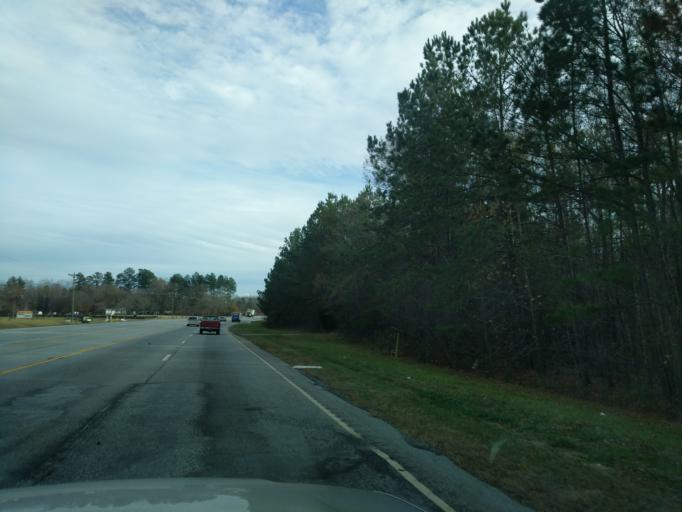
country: US
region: South Carolina
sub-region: Anderson County
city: Williamston
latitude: 34.6062
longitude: -82.3656
